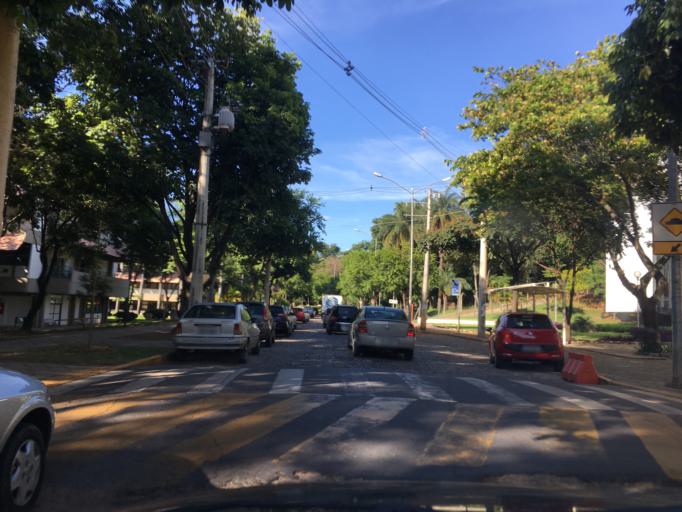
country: BR
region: Minas Gerais
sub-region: Belo Horizonte
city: Belo Horizonte
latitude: -19.8670
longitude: -43.9668
